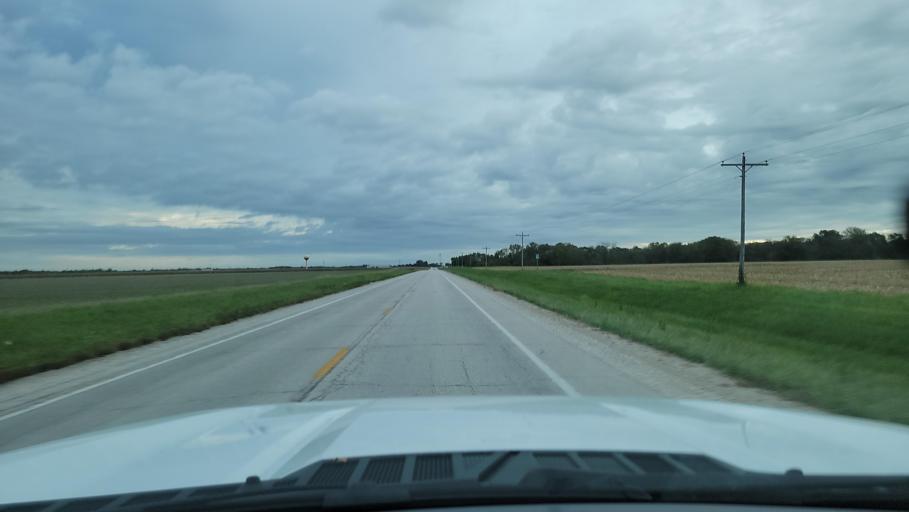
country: US
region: Illinois
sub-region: Schuyler County
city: Rushville
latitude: 40.1051
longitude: -90.5935
